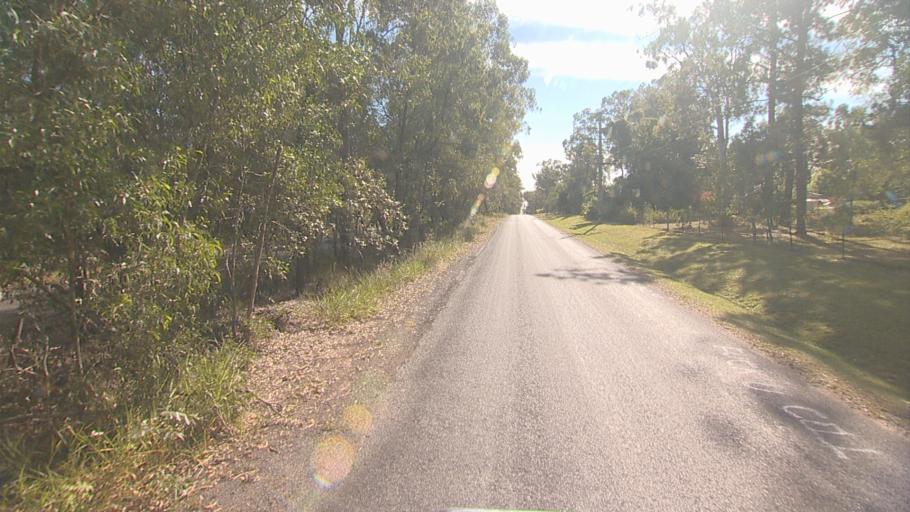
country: AU
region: Queensland
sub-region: Brisbane
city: Forest Lake
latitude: -27.6543
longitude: 152.9830
